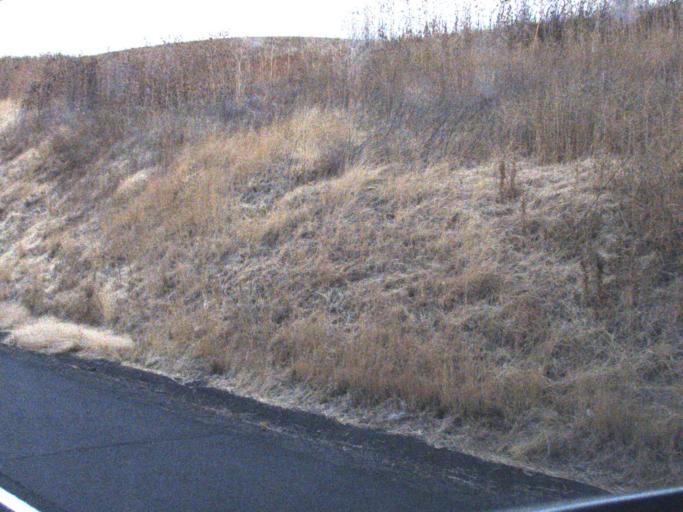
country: US
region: Washington
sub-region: Whitman County
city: Colfax
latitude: 46.9300
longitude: -117.3385
